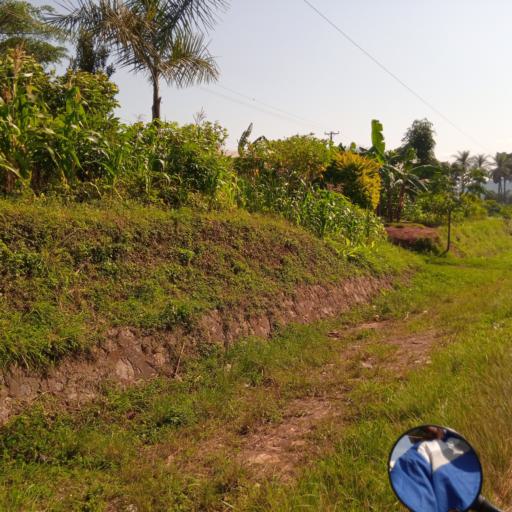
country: UG
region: Central Region
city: Masaka
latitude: -0.3632
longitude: 31.7182
